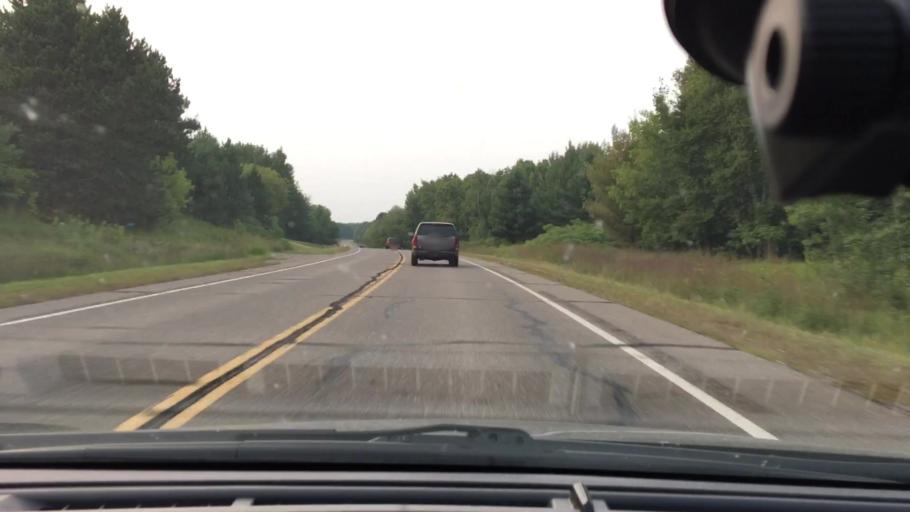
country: US
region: Minnesota
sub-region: Crow Wing County
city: Crosby
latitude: 46.4357
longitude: -93.8740
